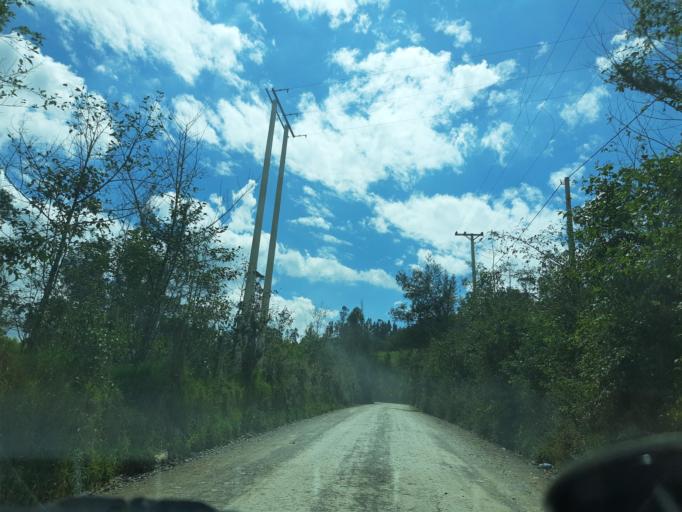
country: CO
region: Boyaca
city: Chiquinquira
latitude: 5.6117
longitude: -73.7715
